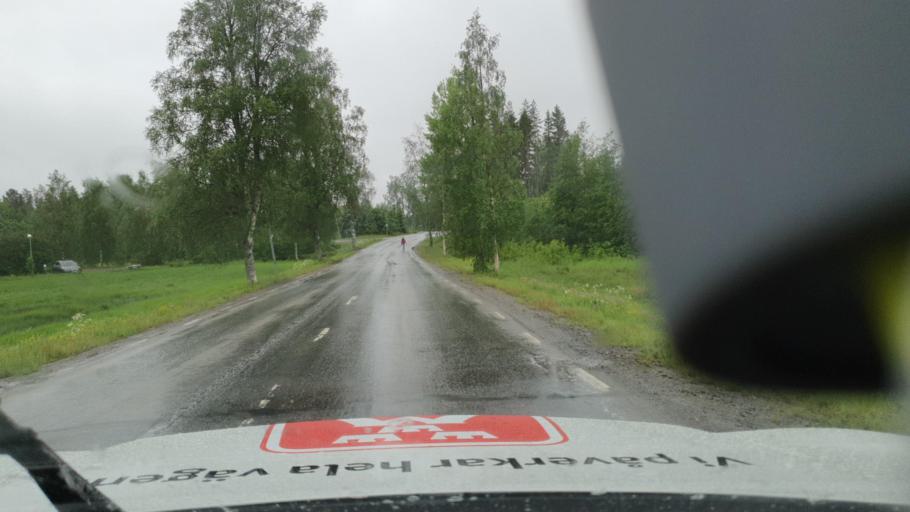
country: SE
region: Vaesterbotten
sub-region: Umea Kommun
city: Saevar
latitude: 64.0278
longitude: 20.4808
